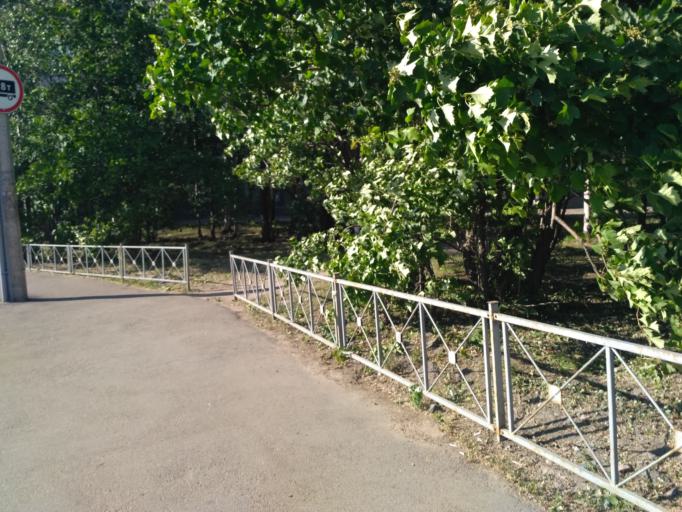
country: RU
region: Leningrad
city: Kalininskiy
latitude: 59.9797
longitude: 30.3817
